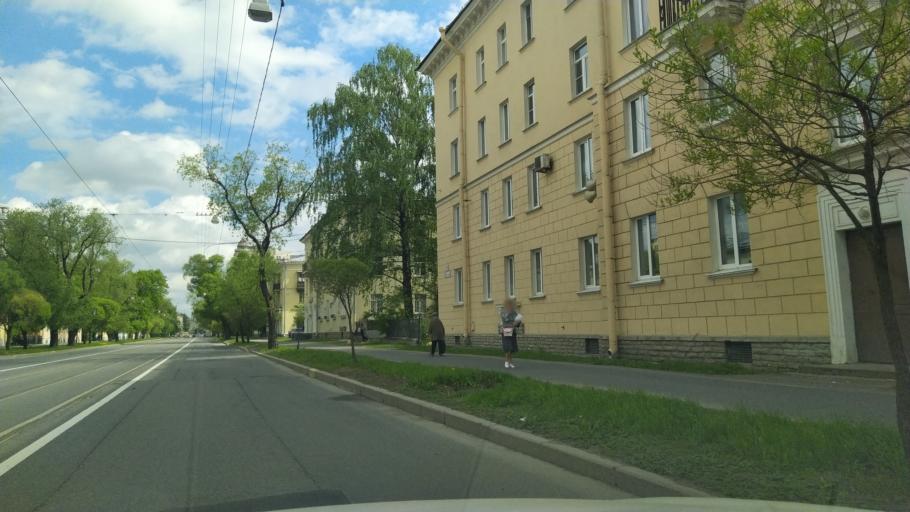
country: RU
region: St.-Petersburg
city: Novaya Derevnya
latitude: 59.9845
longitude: 30.2787
